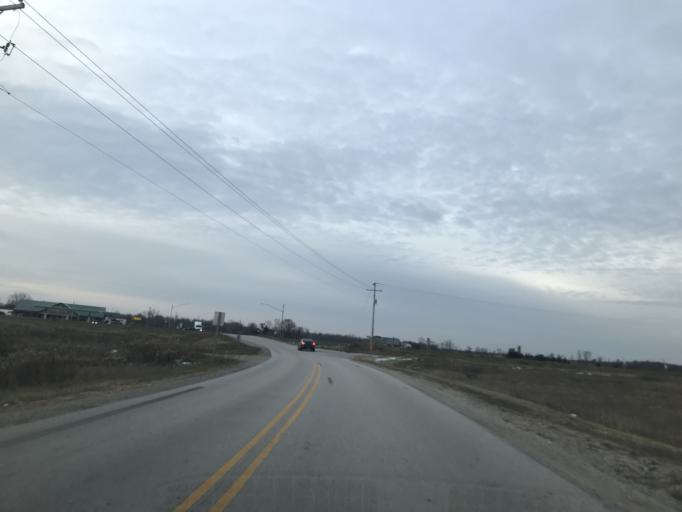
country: US
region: Wisconsin
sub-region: Marinette County
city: Peshtigo
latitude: 45.0525
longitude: -87.8001
